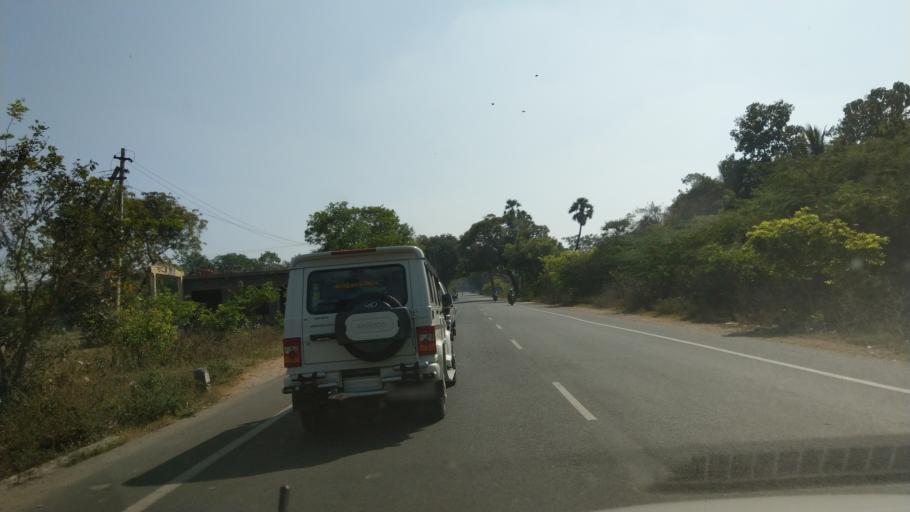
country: IN
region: Tamil Nadu
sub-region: Vellore
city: Arcot
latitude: 12.8801
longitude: 79.3163
